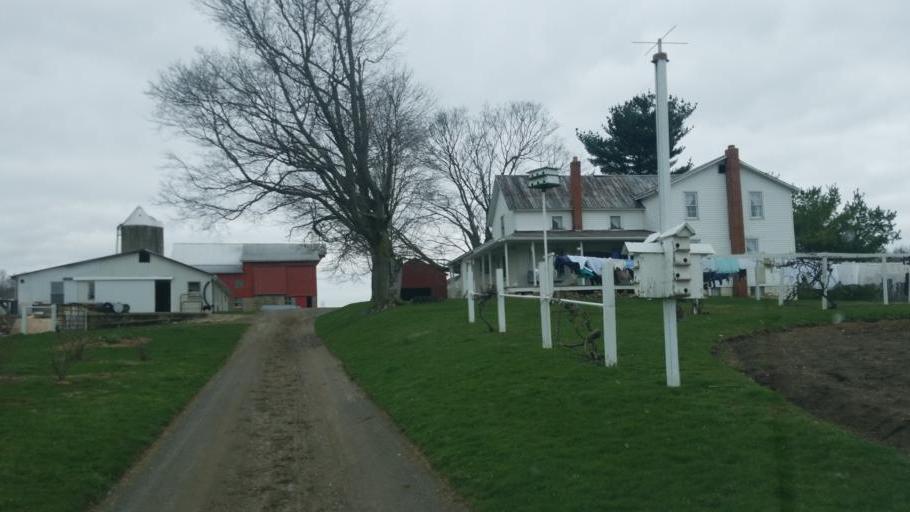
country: US
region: Ohio
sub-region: Knox County
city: Fredericktown
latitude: 40.5085
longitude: -82.6201
